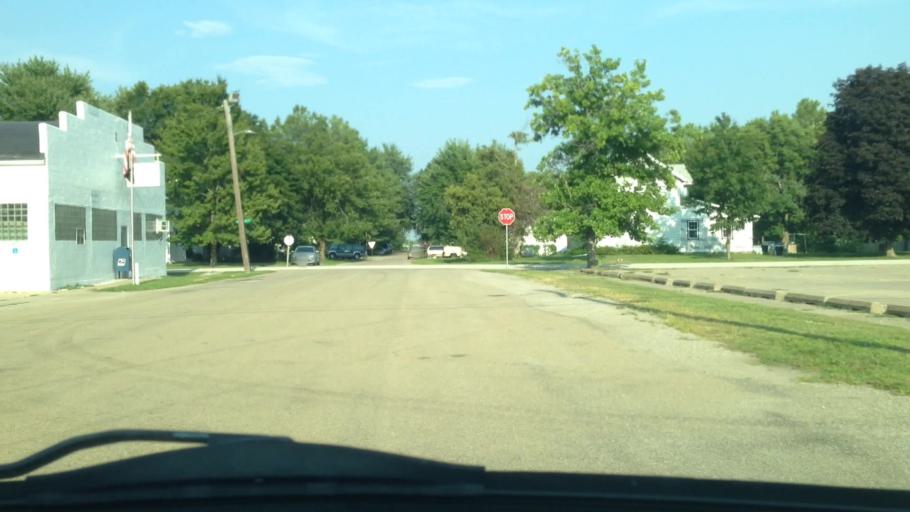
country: US
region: Iowa
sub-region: Henry County
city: Winfield
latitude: 41.2150
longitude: -91.5382
